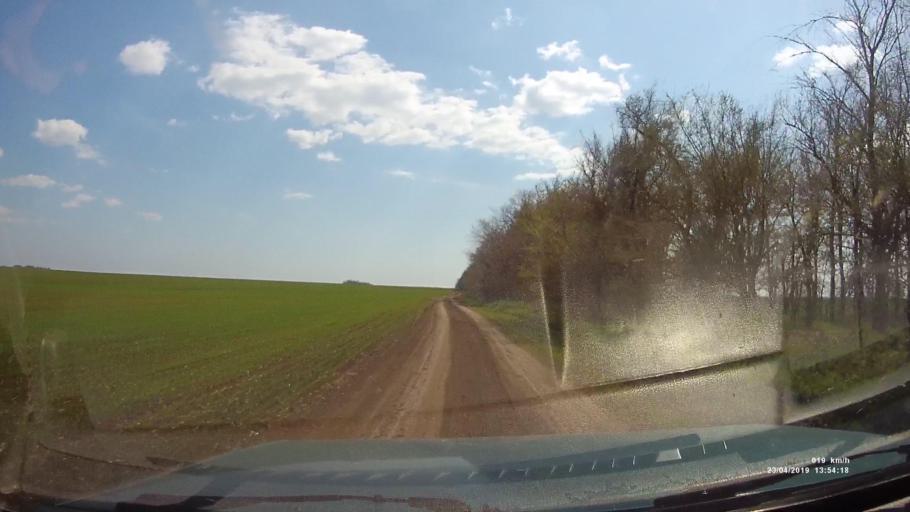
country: RU
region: Rostov
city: Remontnoye
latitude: 46.5989
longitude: 42.9527
